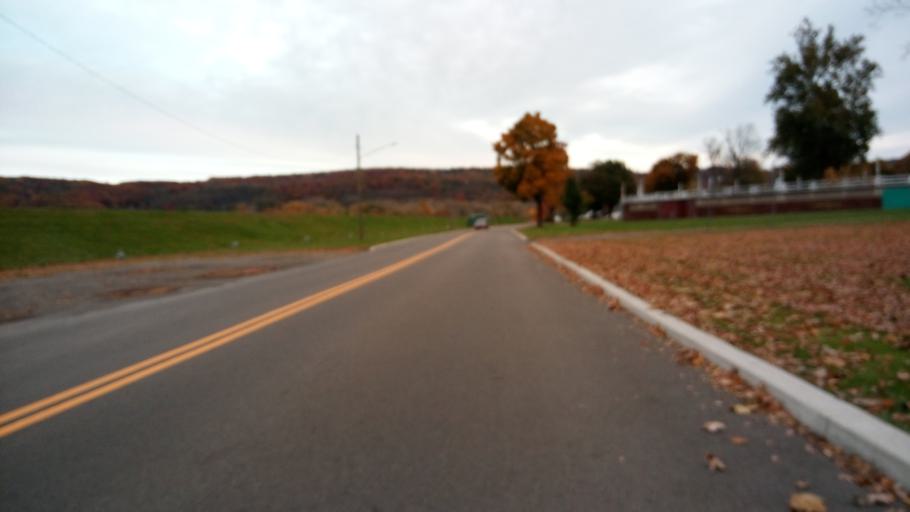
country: US
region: New York
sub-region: Chemung County
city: Elmira
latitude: 42.0863
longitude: -76.7946
